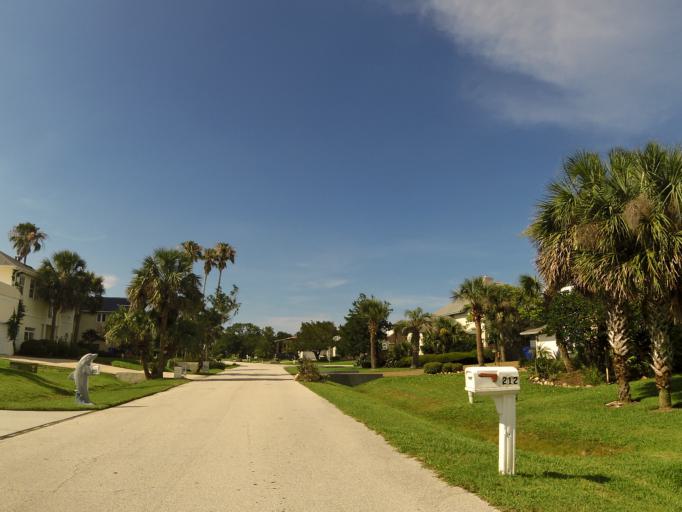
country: US
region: Florida
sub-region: Saint Johns County
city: Villano Beach
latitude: 29.9134
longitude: -81.2967
